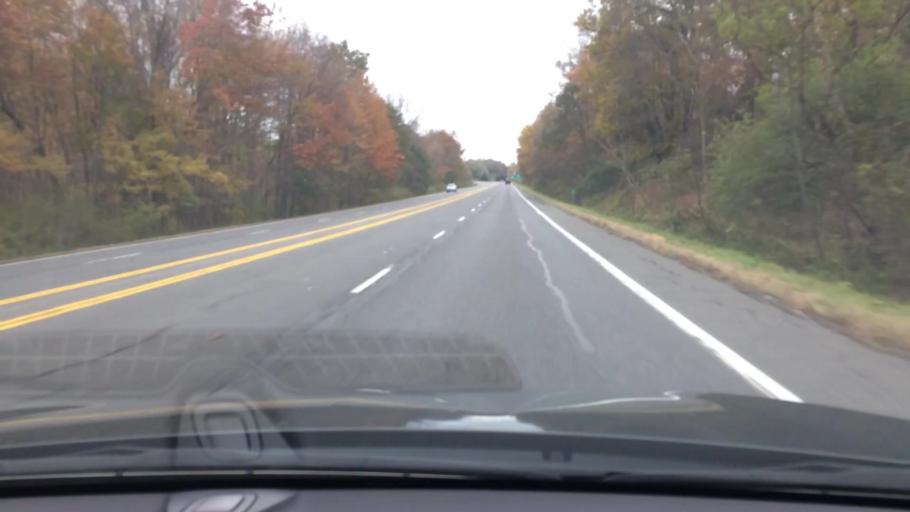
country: US
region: New York
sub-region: Columbia County
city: Valatie
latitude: 42.4146
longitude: -73.6909
